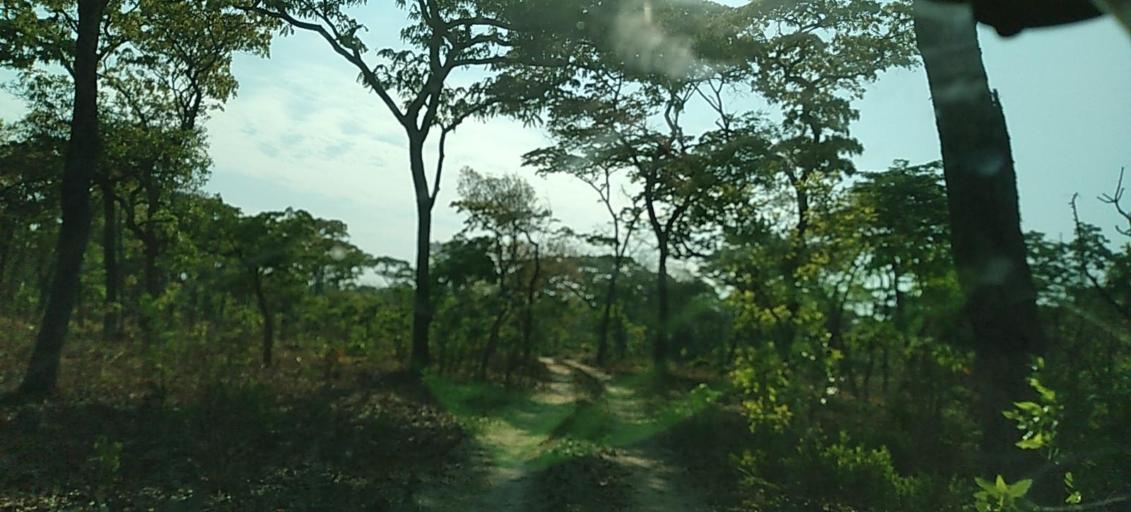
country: ZM
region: North-Western
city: Kalengwa
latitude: -13.2350
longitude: 25.0619
